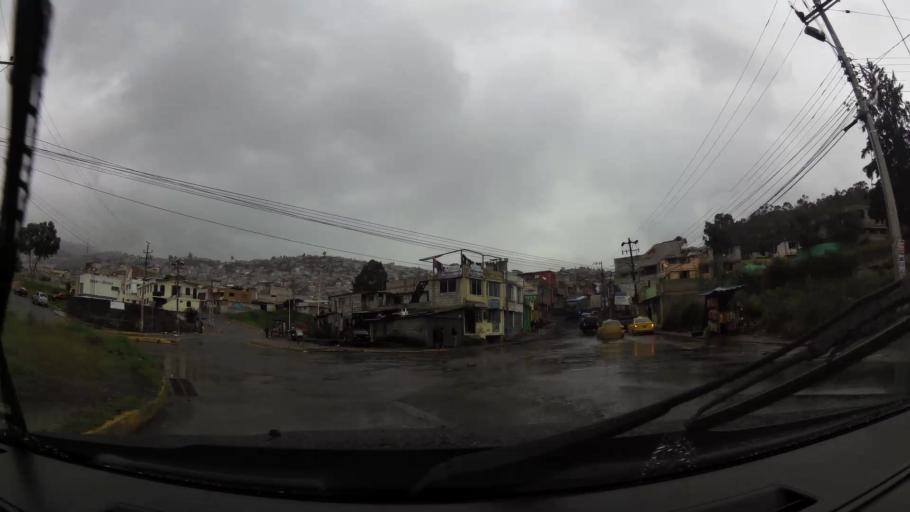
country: EC
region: Pichincha
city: Quito
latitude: -0.0940
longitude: -78.4976
